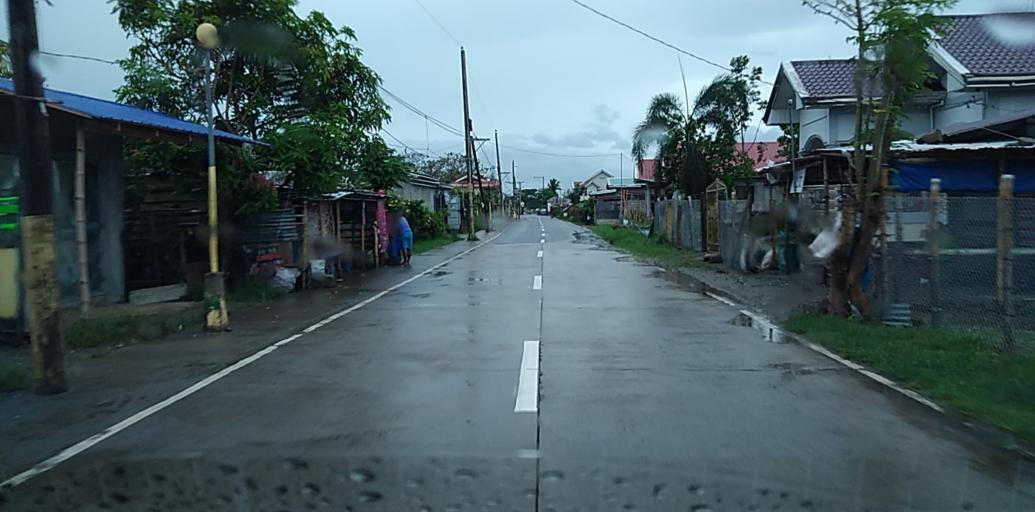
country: PH
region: Central Luzon
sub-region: Province of Pampanga
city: Salapungan
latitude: 15.1347
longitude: 120.9086
